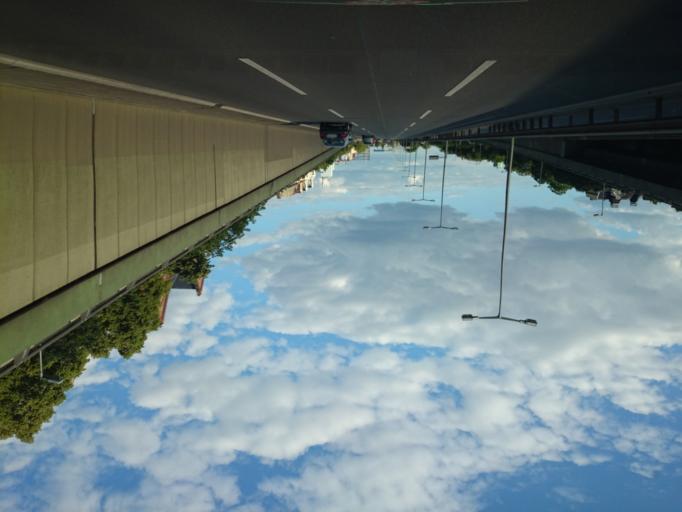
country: DE
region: Berlin
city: Friedenau
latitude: 52.4675
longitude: 13.3385
